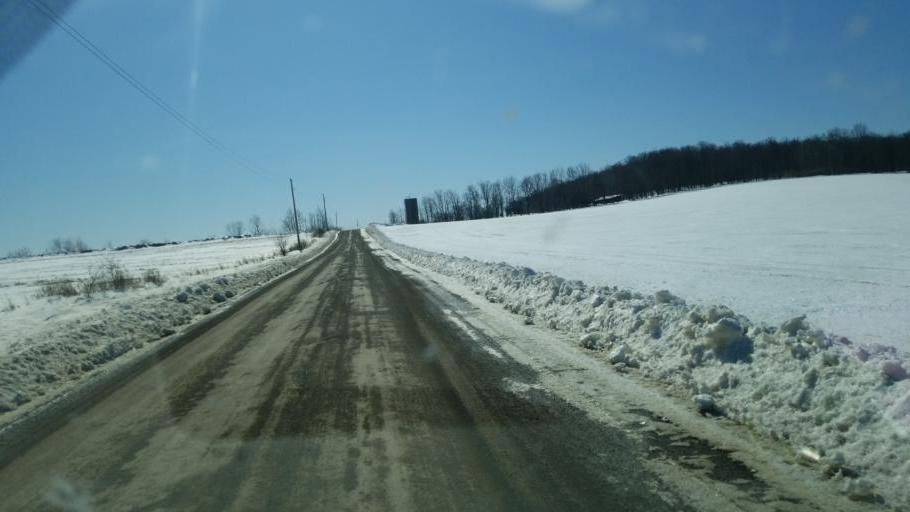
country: US
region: New York
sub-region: Allegany County
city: Alfred
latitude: 42.2676
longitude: -77.7322
